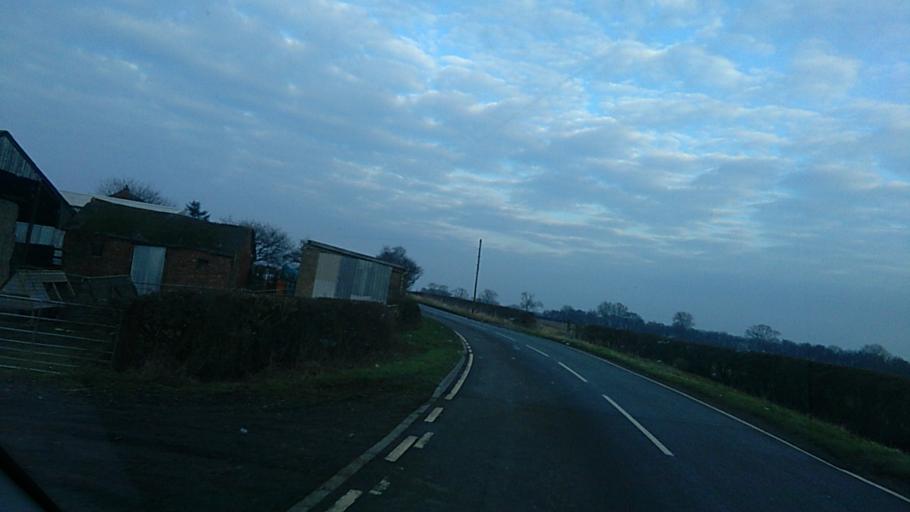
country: GB
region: England
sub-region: Leicestershire
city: Melton Mowbray
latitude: 52.8274
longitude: -0.8993
